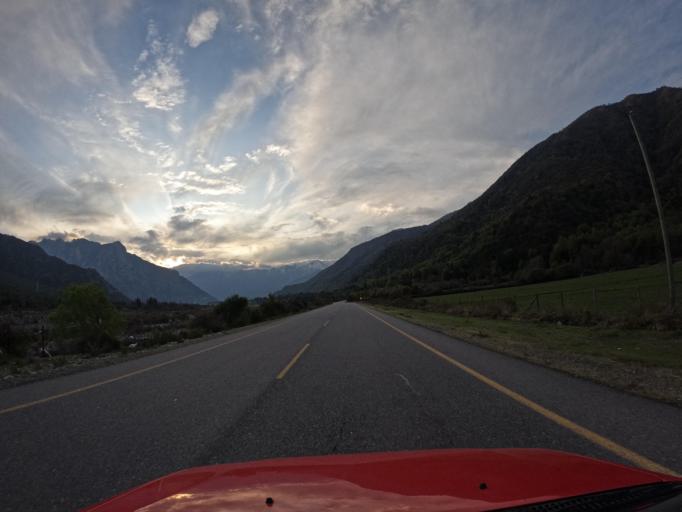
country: CL
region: Maule
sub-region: Provincia de Linares
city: Colbun
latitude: -35.7201
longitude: -71.0316
